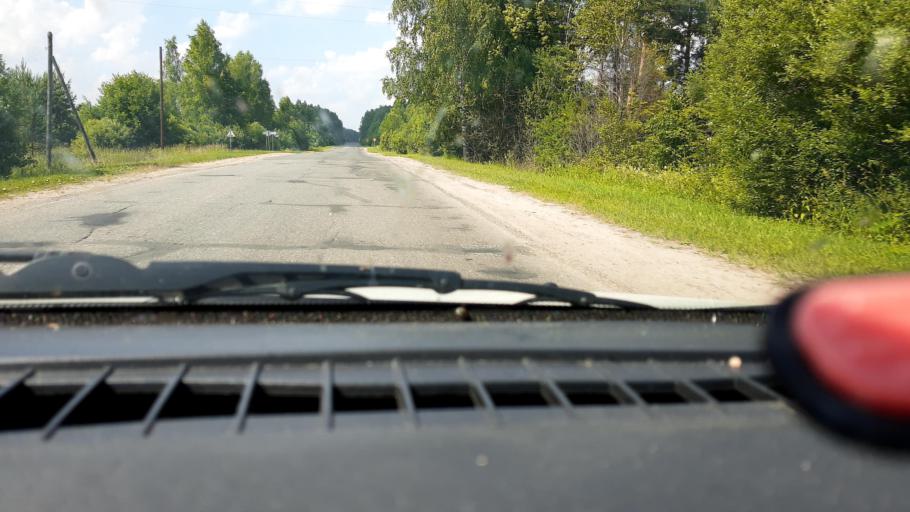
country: RU
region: Nizjnij Novgorod
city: Prudy
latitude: 57.4051
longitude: 46.0773
